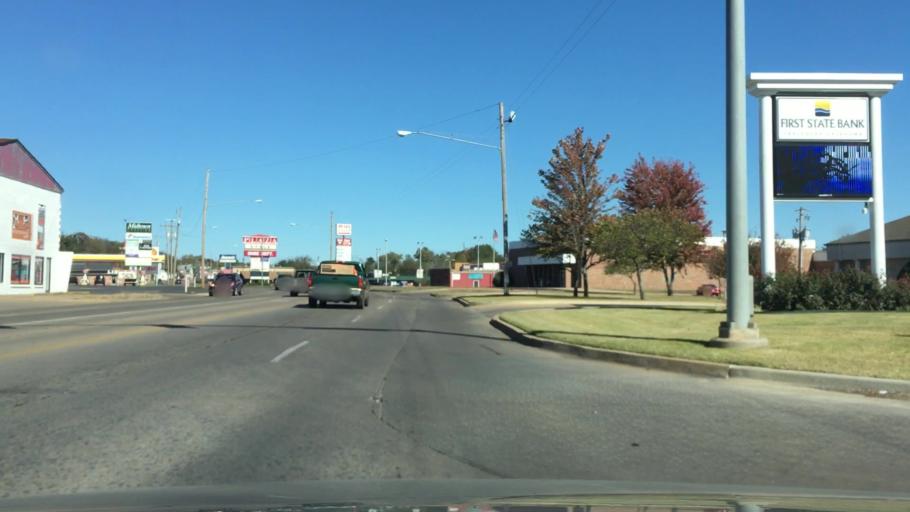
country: US
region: Oklahoma
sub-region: Cherokee County
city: Tahlequah
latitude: 35.9009
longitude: -94.9747
